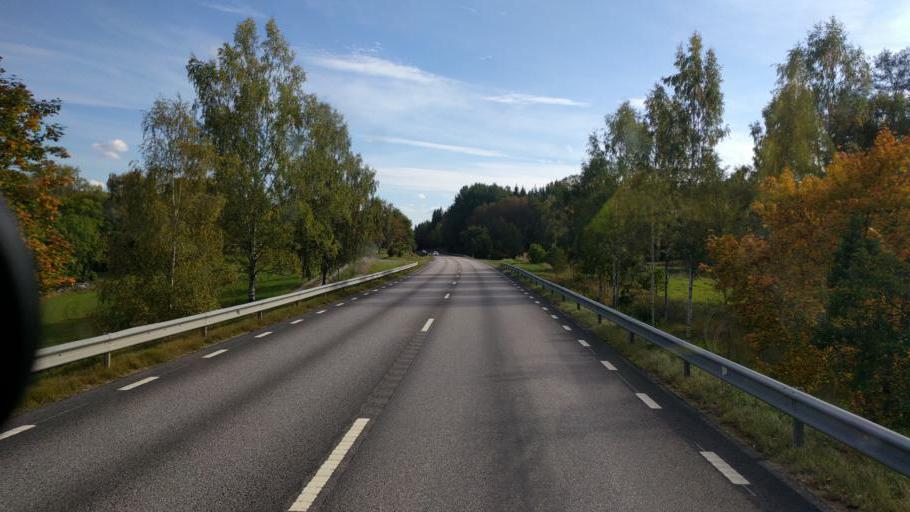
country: SE
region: OEstergoetland
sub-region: Kinda Kommun
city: Kisa
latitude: 57.9145
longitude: 15.6870
